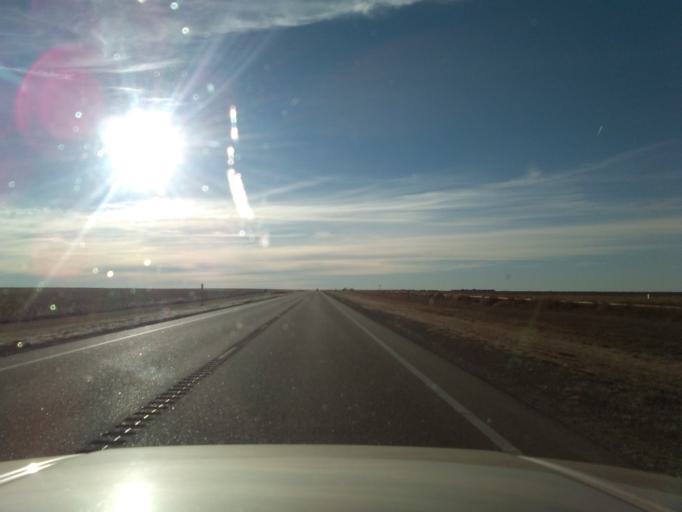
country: US
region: Kansas
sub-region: Sheridan County
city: Hoxie
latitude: 39.5240
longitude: -100.6145
